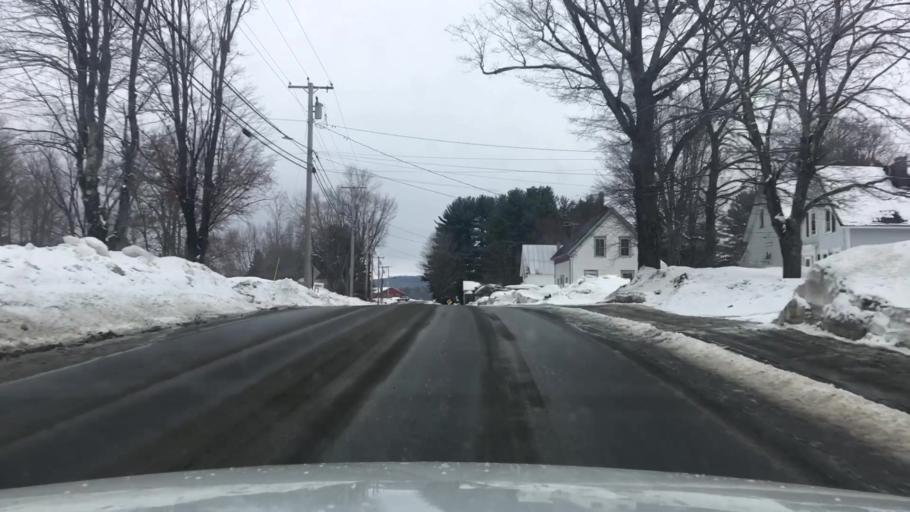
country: US
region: Maine
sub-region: Somerset County
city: Norridgewock
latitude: 44.7095
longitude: -69.7912
